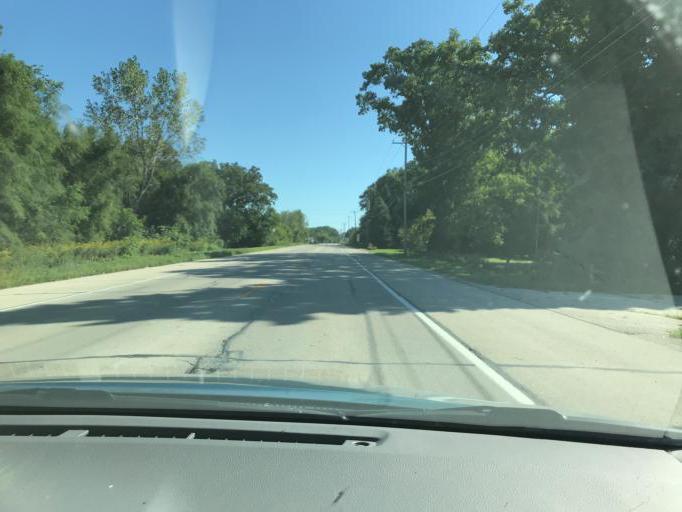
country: US
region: Illinois
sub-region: Lake County
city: Winthrop Harbor
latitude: 42.4984
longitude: -87.8225
